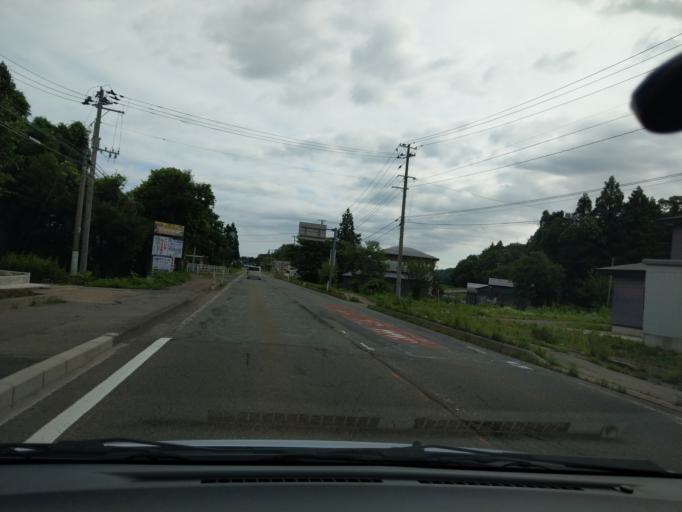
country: JP
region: Akita
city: Yokotemachi
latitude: 39.3481
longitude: 140.5617
